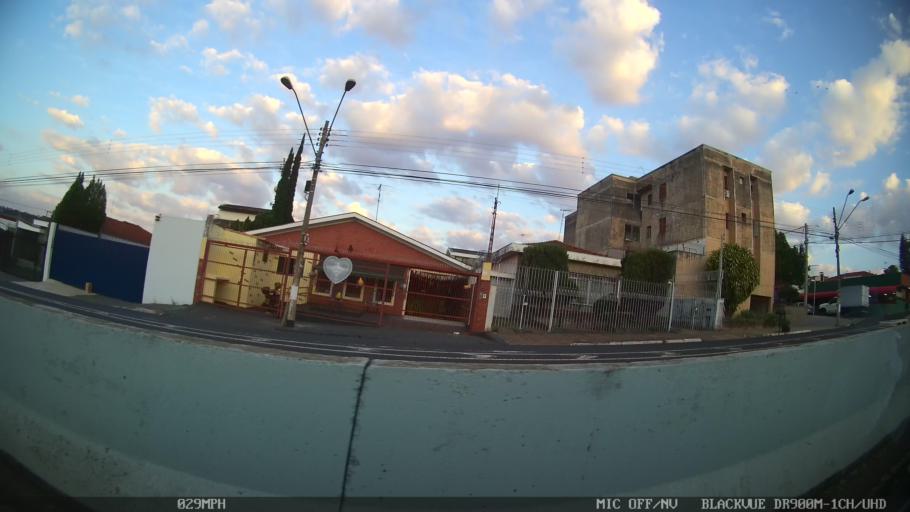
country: BR
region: Sao Paulo
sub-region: Ribeirao Preto
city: Ribeirao Preto
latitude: -21.1725
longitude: -47.7940
